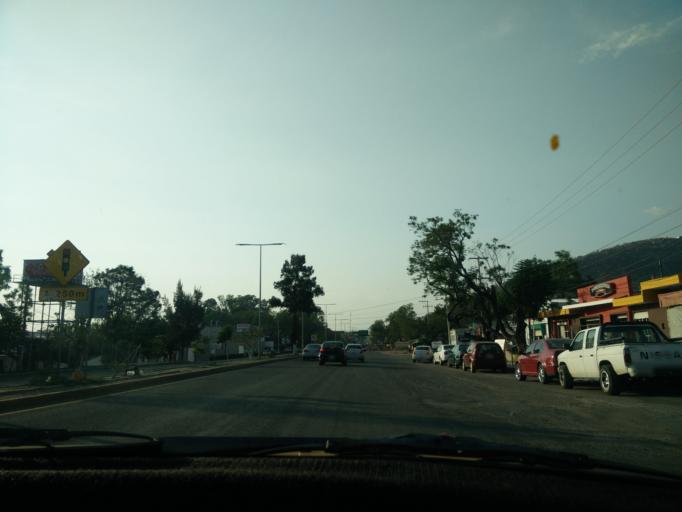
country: MX
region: Oaxaca
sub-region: Santa Maria Atzompa
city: San Jeronimo Yahuiche
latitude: 17.0994
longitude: -96.7508
